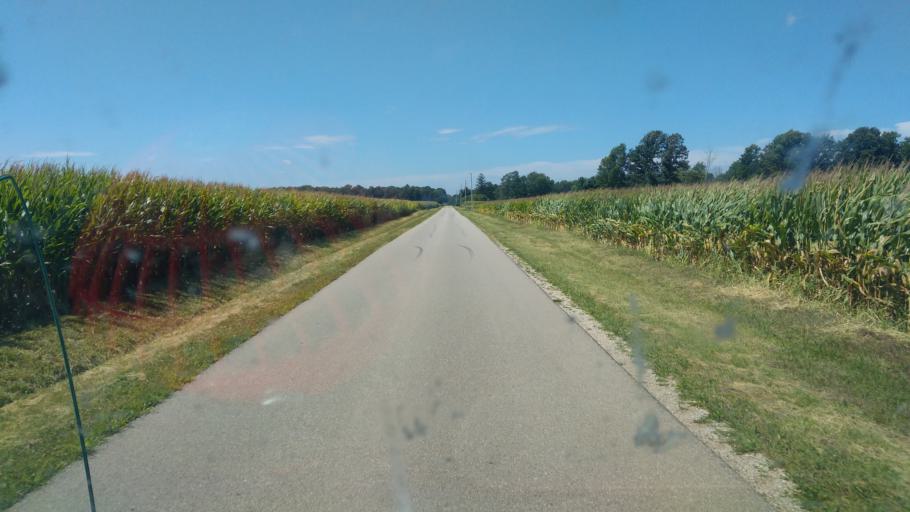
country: US
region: Ohio
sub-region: Crawford County
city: Galion
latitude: 40.7697
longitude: -82.8657
